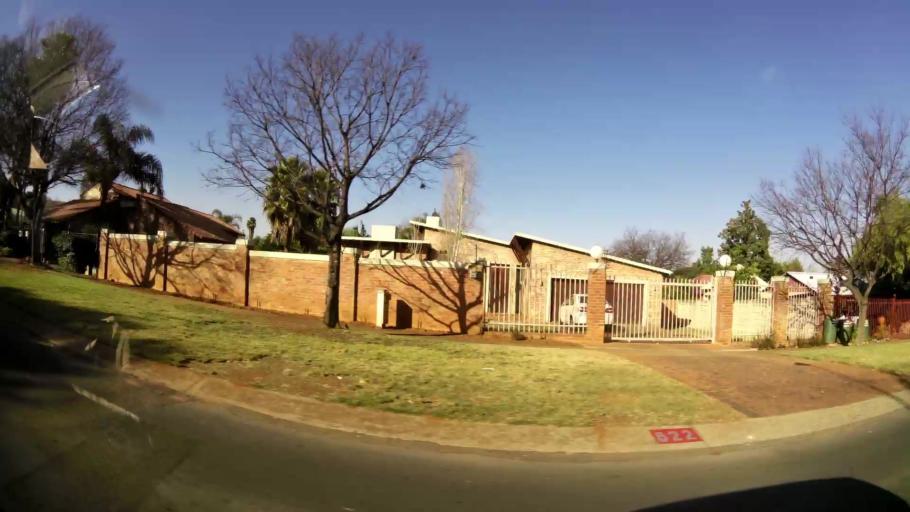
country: ZA
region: Gauteng
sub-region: City of Tshwane Metropolitan Municipality
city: Pretoria
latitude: -25.7005
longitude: 28.2560
